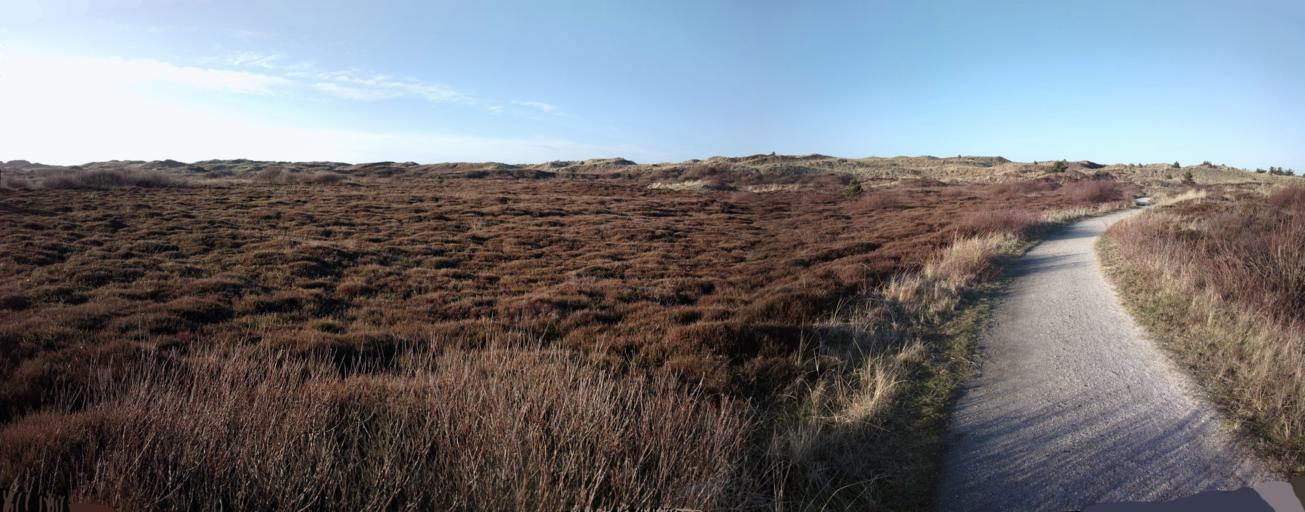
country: NL
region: North Holland
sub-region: Gemeente Texel
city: Den Burg
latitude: 53.0795
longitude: 4.7459
